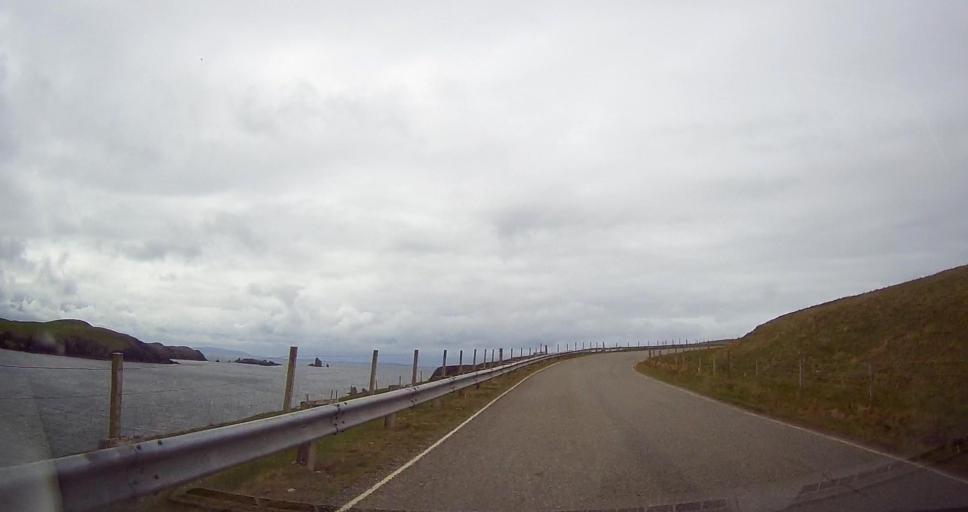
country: GB
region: Scotland
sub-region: Shetland Islands
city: Lerwick
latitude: 60.4859
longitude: -1.5004
